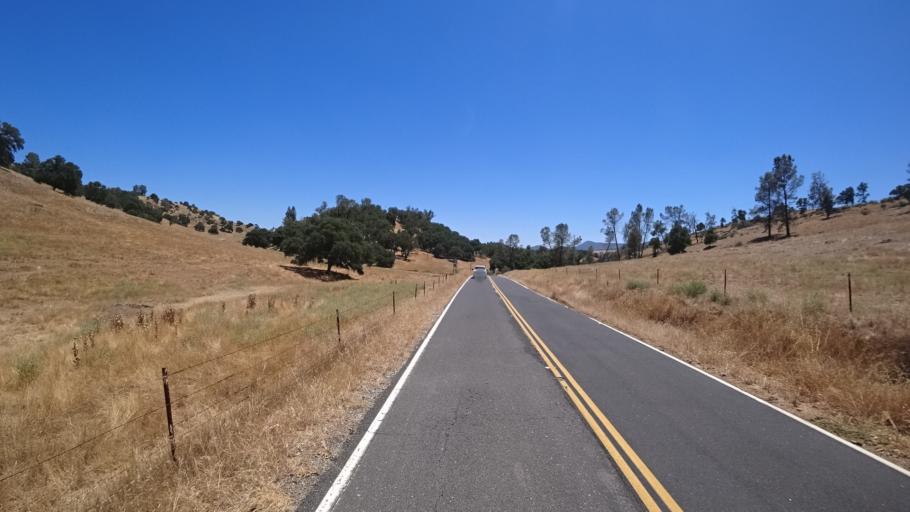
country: US
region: California
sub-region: Calaveras County
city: San Andreas
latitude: 38.1494
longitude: -120.6606
